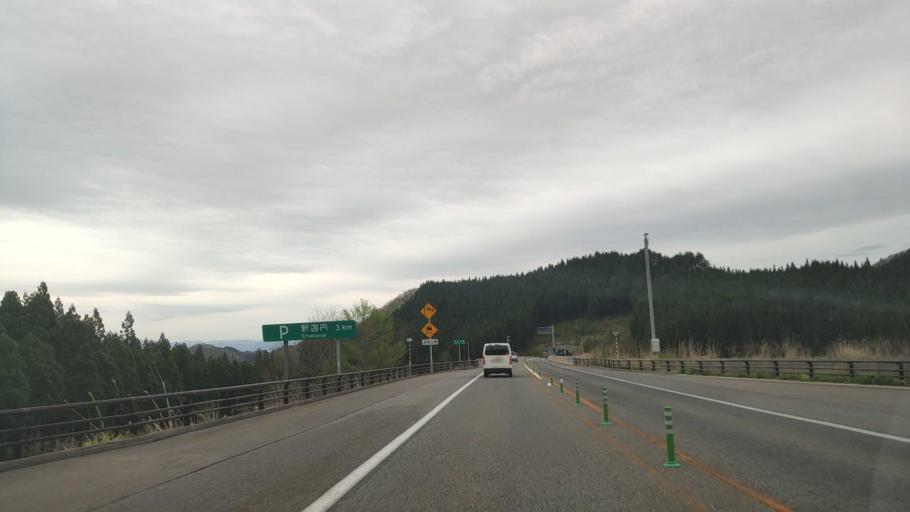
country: JP
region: Akita
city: Odate
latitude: 40.3279
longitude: 140.6061
